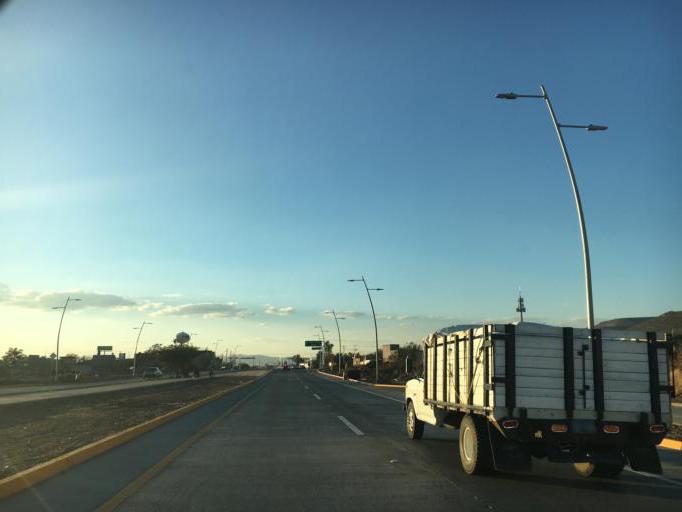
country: MX
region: Guanajuato
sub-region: Leon
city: Fraccionamiento Paraiso Real
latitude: 21.1043
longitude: -101.5780
